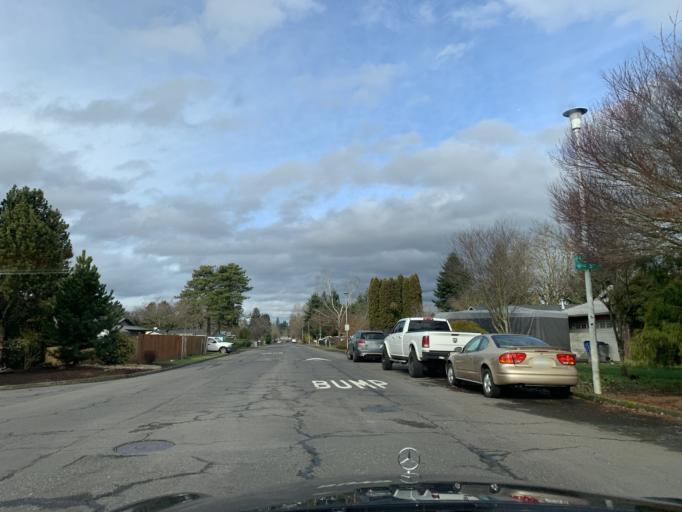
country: US
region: Washington
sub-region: Clark County
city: Mill Plain
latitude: 45.6179
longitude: -122.5138
